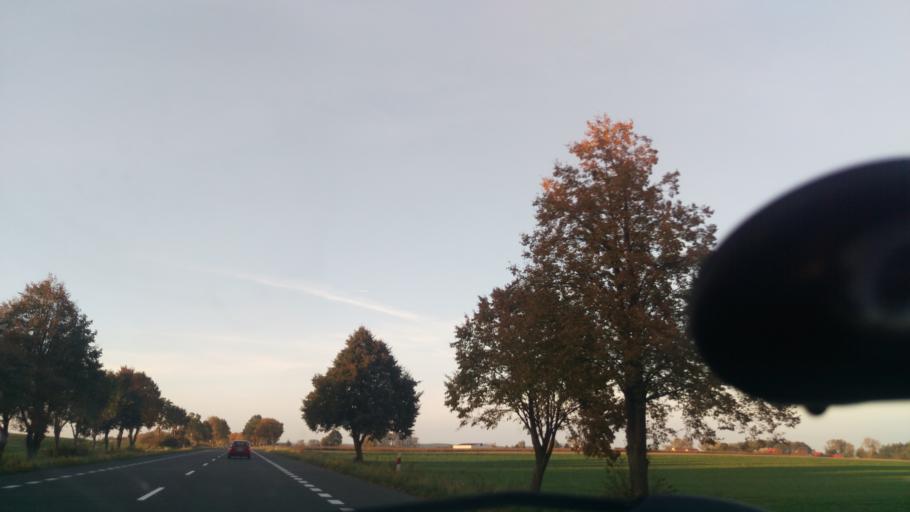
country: PL
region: West Pomeranian Voivodeship
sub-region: Powiat gryfinski
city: Stare Czarnowo
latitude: 53.2239
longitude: 14.7956
